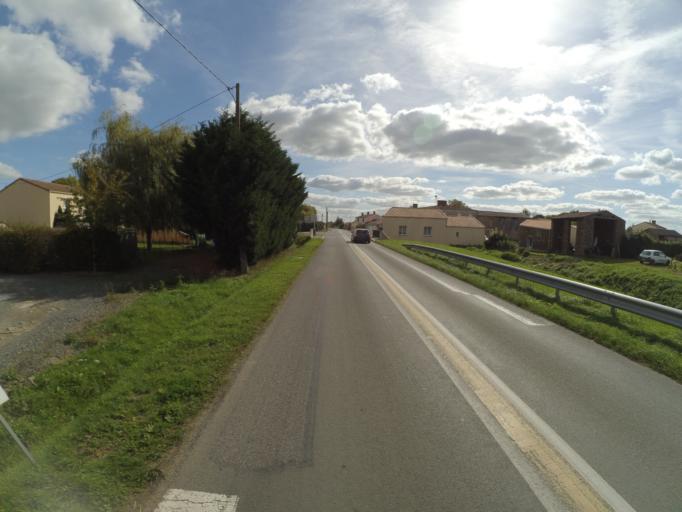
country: FR
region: Pays de la Loire
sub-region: Departement de la Loire-Atlantique
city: La Chapelle-Heulin
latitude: 47.1966
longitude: -1.3469
